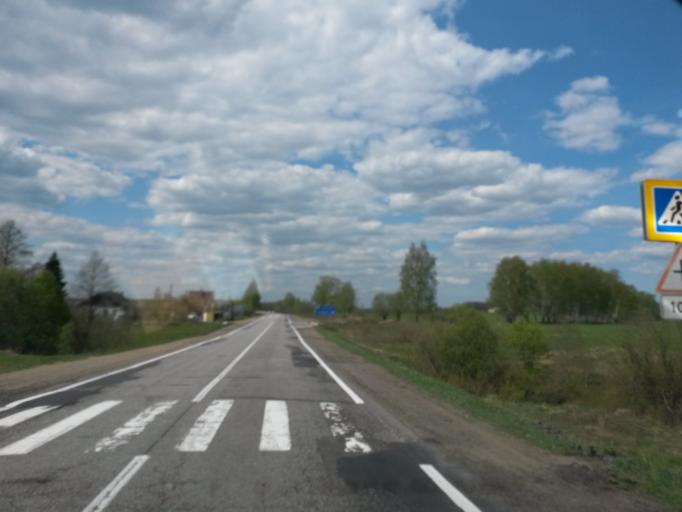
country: RU
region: Jaroslavl
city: Konstantinovskiy
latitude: 57.6697
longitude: 39.6206
